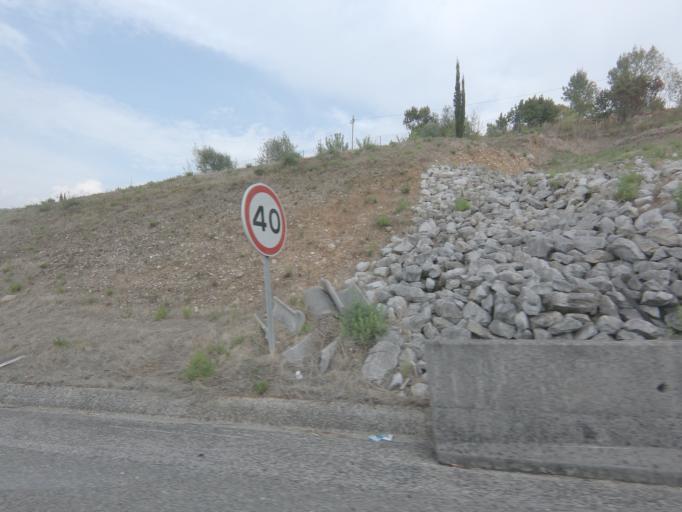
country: PT
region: Coimbra
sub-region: Coimbra
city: Coimbra
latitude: 40.2134
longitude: -8.4461
